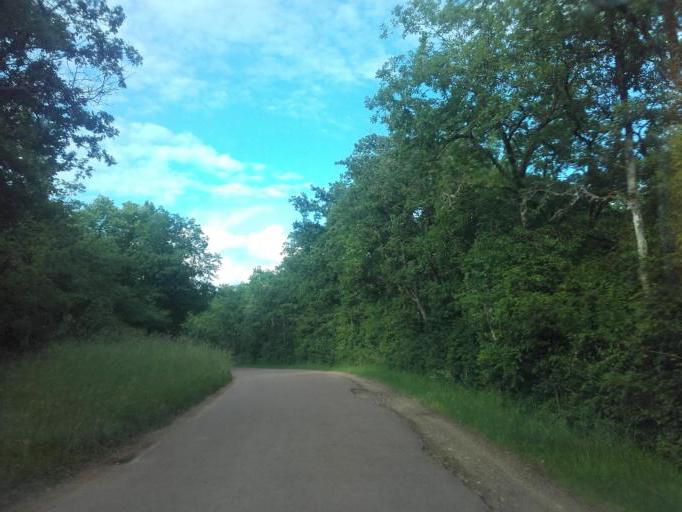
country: FR
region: Bourgogne
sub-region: Departement de Saone-et-Loire
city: Rully
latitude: 46.8451
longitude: 4.7376
